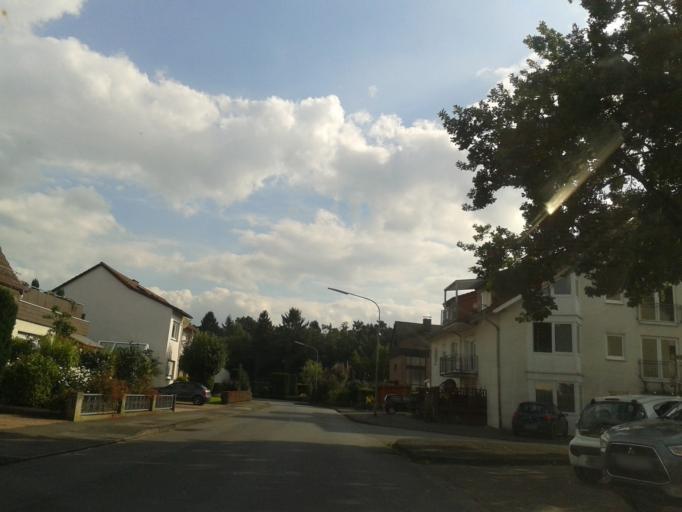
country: DE
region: North Rhine-Westphalia
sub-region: Regierungsbezirk Detmold
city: Schlangen
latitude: 51.8009
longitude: 8.8322
